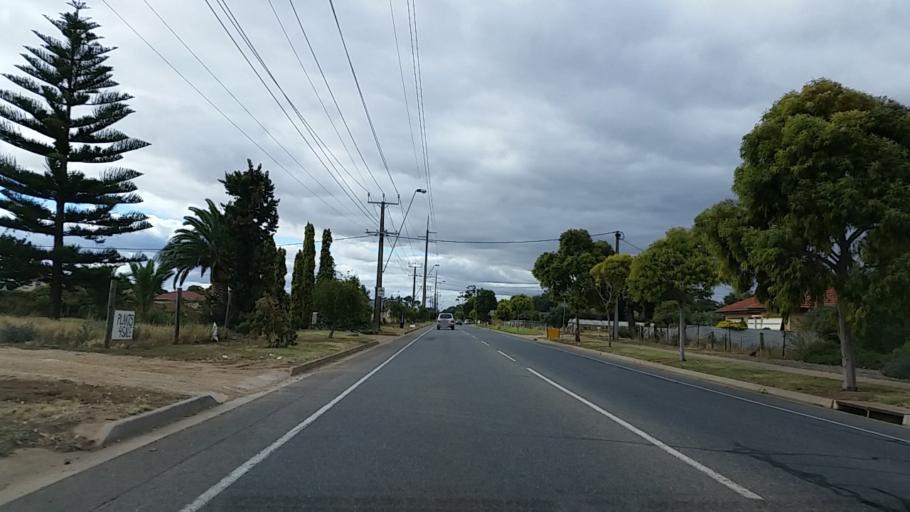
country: AU
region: South Australia
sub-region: Salisbury
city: Salisbury
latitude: -34.7864
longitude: 138.6041
